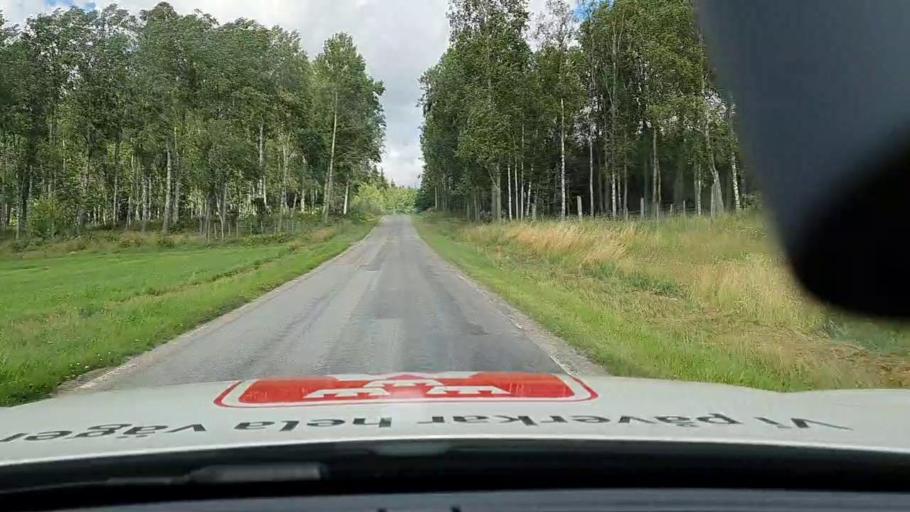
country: SE
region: Vaestra Goetaland
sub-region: Karlsborgs Kommun
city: Molltorp
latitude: 58.6066
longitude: 14.3169
